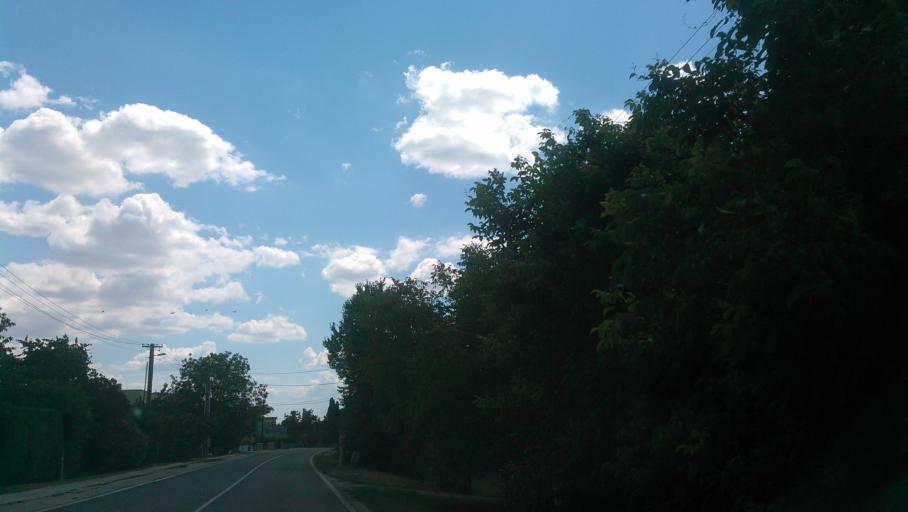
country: SK
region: Trnavsky
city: Vrbove
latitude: 48.5410
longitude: 17.7338
